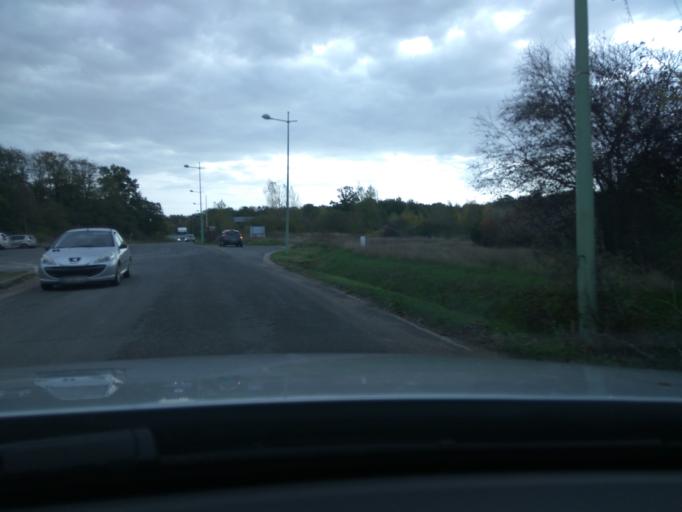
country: FR
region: Bourgogne
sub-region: Departement de la Nievre
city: Cosne-Cours-sur-Loire
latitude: 47.3794
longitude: 2.9075
